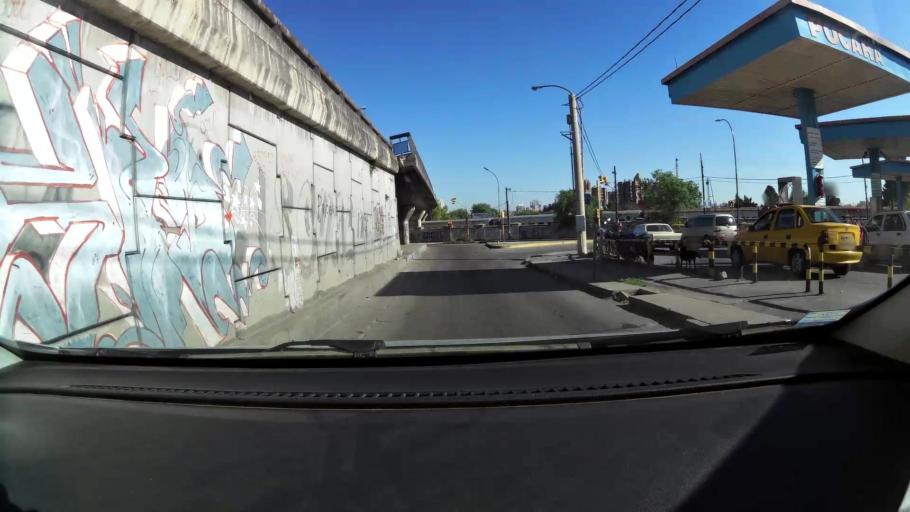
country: AR
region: Cordoba
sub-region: Departamento de Capital
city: Cordoba
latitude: -31.4255
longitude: -64.1703
